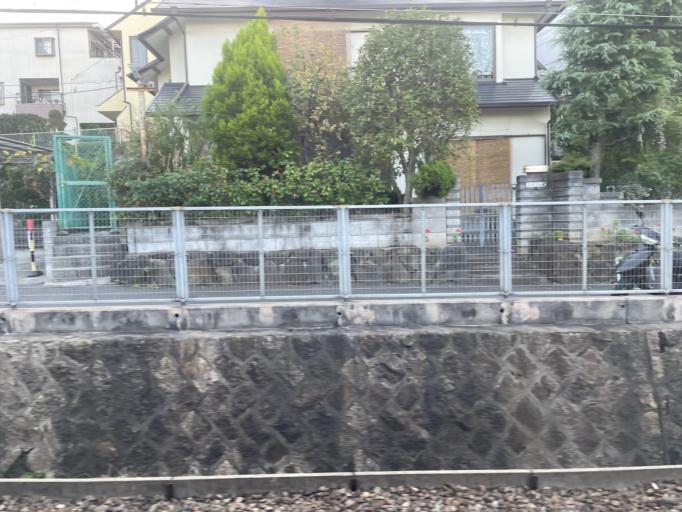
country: JP
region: Osaka
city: Daitocho
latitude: 34.6690
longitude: 135.6479
